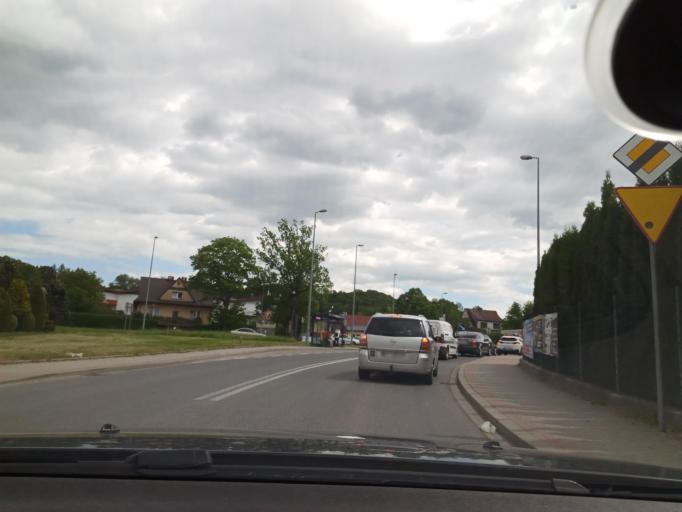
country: PL
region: Lesser Poland Voivodeship
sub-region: Powiat limanowski
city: Limanowa
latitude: 49.7370
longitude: 20.4010
